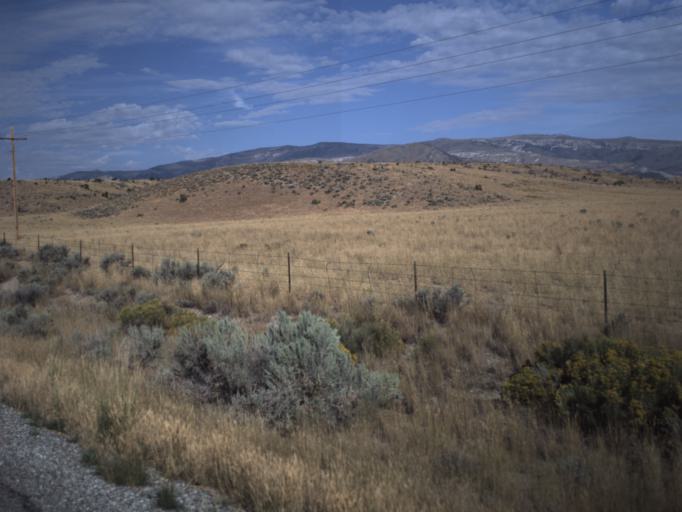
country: US
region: Idaho
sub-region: Cassia County
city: Burley
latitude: 41.8150
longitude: -113.2164
